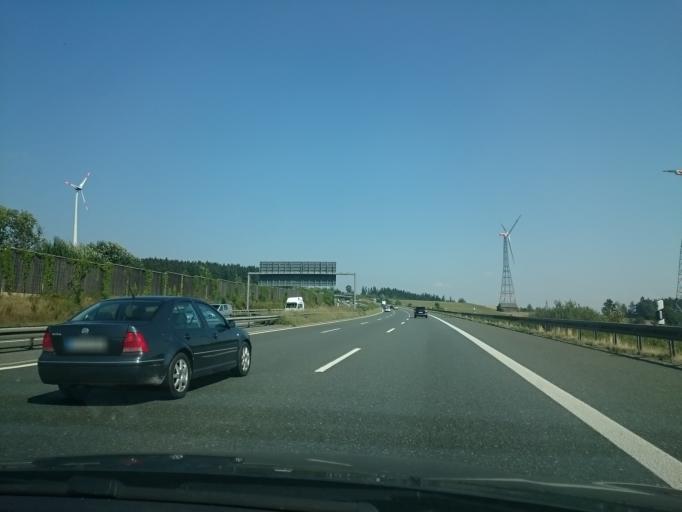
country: DE
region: Bavaria
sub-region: Upper Franconia
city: Munchberg
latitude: 50.2141
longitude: 11.7814
